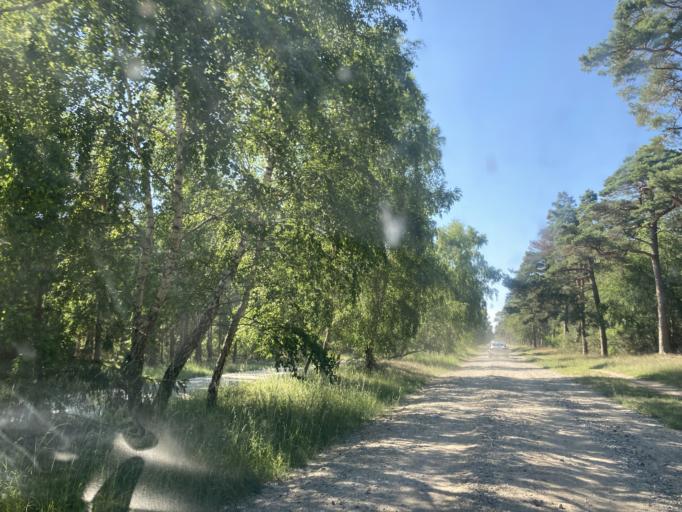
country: DK
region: Capital Region
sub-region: Halsnaes Kommune
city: Frederiksvaerk
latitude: 56.0153
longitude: 12.0148
